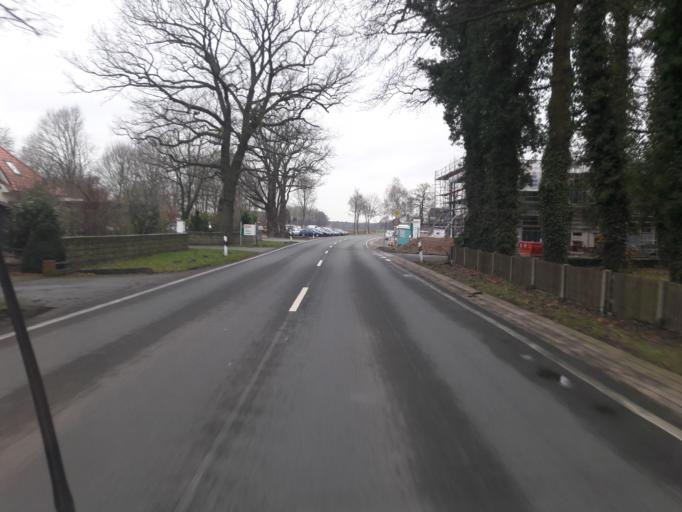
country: DE
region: Lower Saxony
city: Warmsen
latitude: 52.3794
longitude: 8.8474
